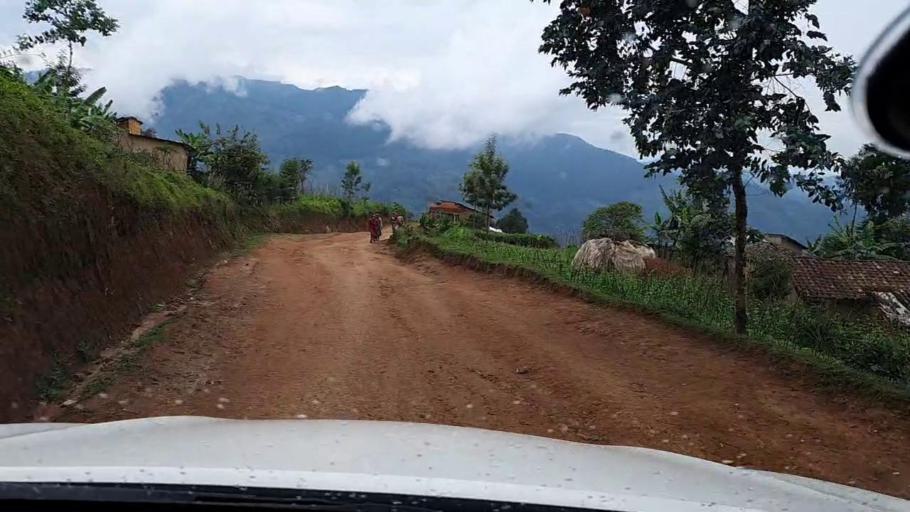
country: RW
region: Southern Province
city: Nzega
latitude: -2.3813
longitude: 29.2401
